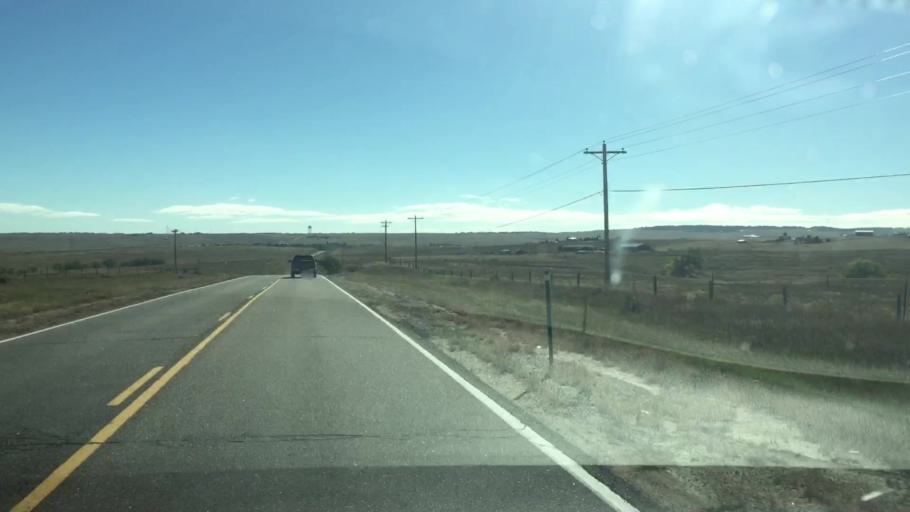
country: US
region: Colorado
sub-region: Elbert County
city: Kiowa
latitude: 39.3525
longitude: -104.4981
